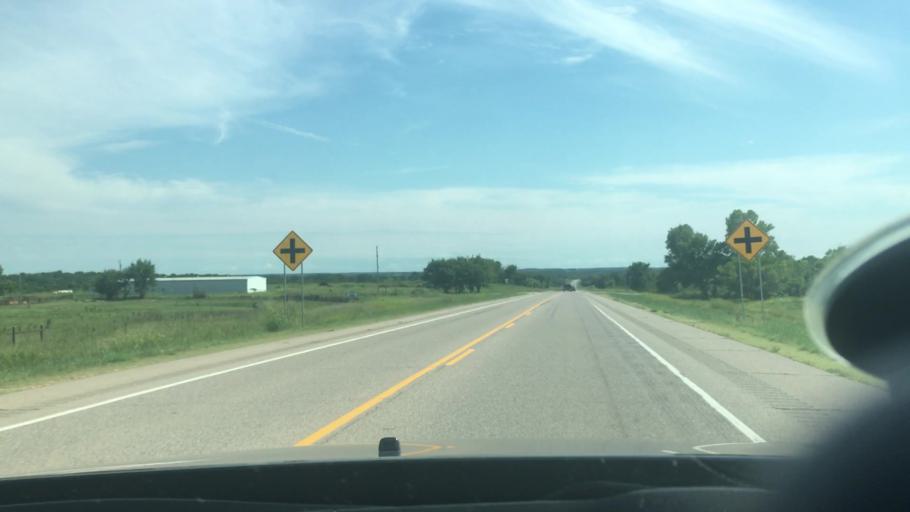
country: US
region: Oklahoma
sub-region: Seminole County
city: Maud
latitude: 35.0889
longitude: -96.6788
